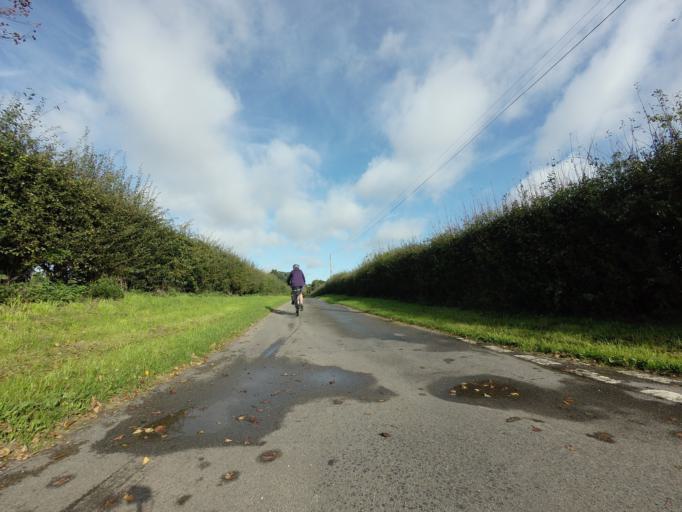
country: GB
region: England
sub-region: Norfolk
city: Fakenham
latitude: 52.8835
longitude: 0.6842
